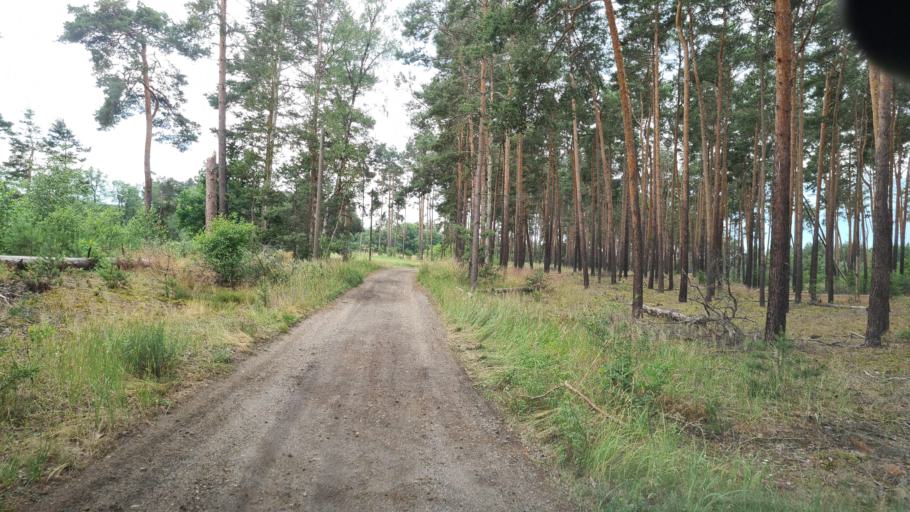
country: DE
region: Brandenburg
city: Crinitz
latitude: 51.6650
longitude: 13.7940
